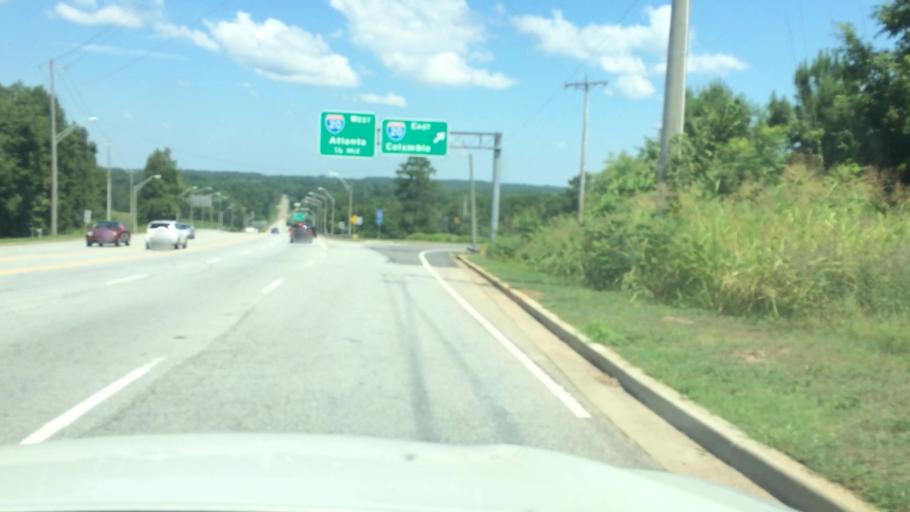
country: US
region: South Carolina
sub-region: Aiken County
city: North Augusta
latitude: 33.5385
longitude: -81.9898
